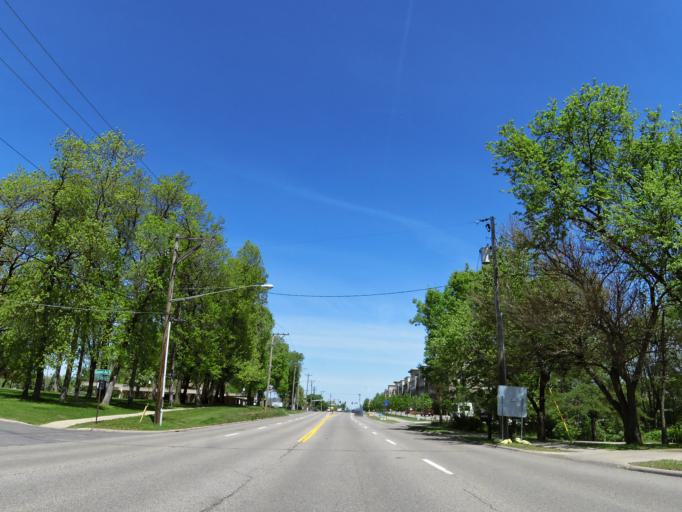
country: US
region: Minnesota
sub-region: Hennepin County
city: Bloomington
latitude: 44.8169
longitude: -93.3106
